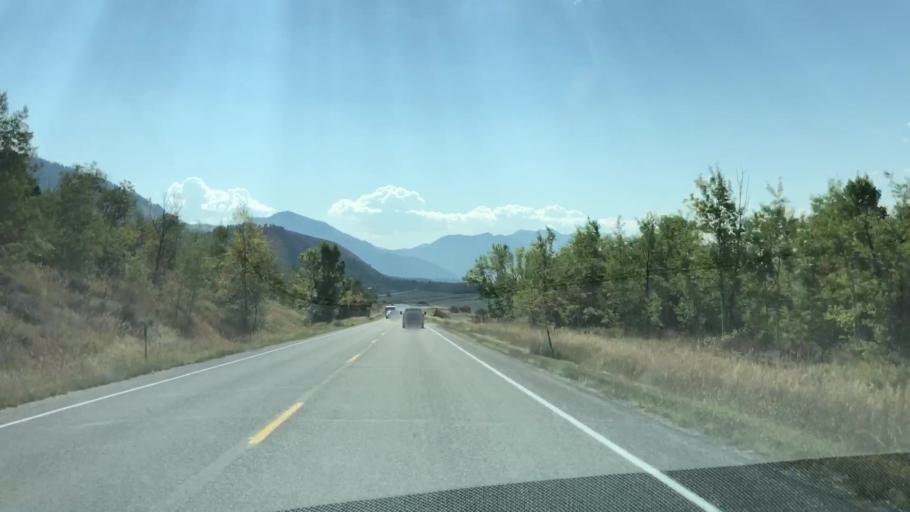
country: US
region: Wyoming
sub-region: Teton County
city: Hoback
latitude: 43.2230
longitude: -111.0761
